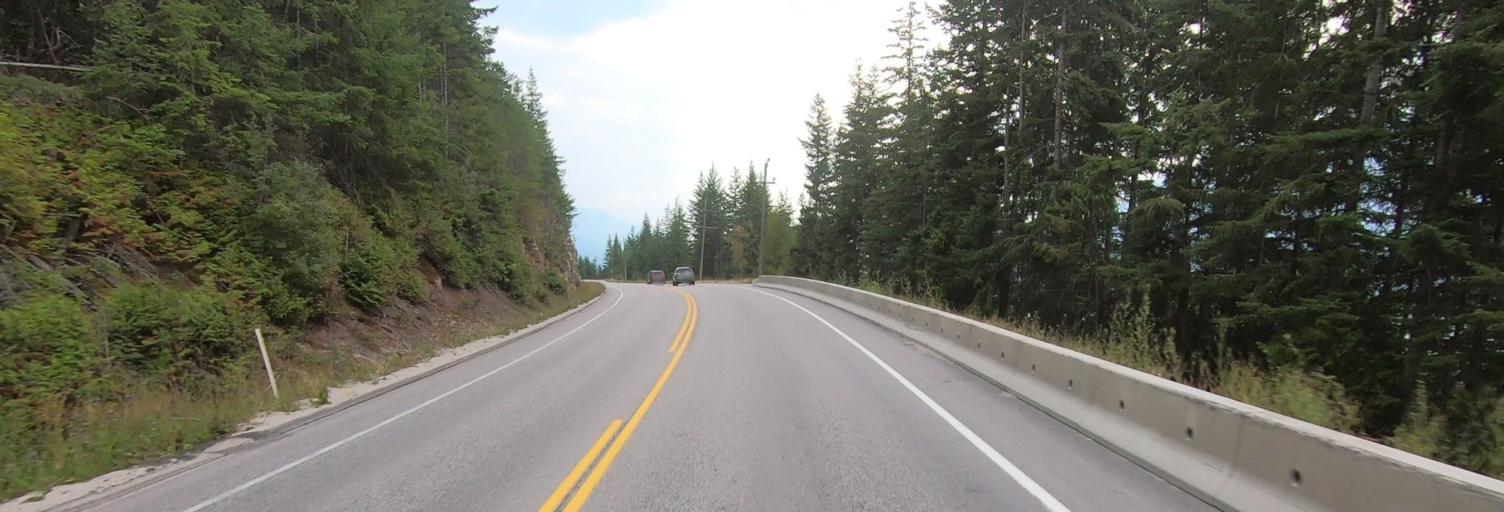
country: CA
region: British Columbia
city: Sicamous
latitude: 50.8244
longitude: -119.0299
